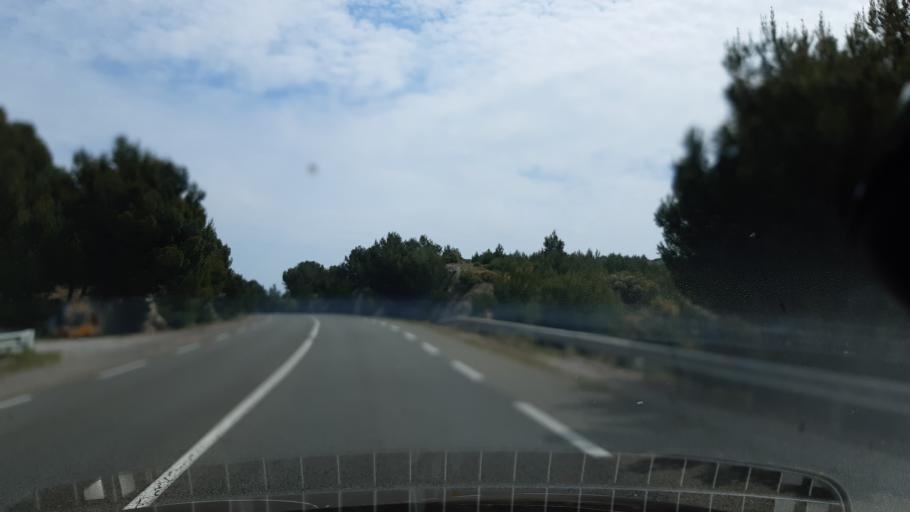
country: FR
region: Languedoc-Roussillon
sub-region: Departement de l'Aude
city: Gruissan
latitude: 43.1215
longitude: 3.0761
